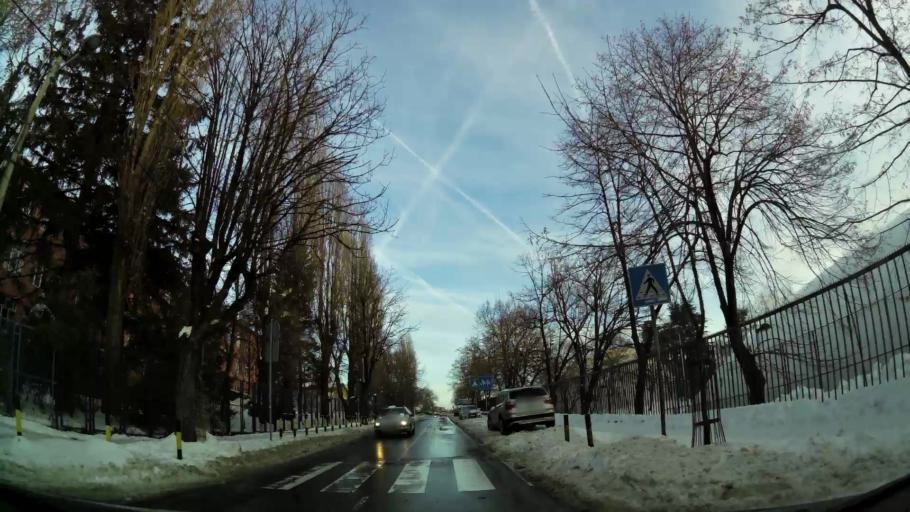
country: RS
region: Central Serbia
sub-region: Belgrade
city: Palilula
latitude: 44.7953
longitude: 20.5095
